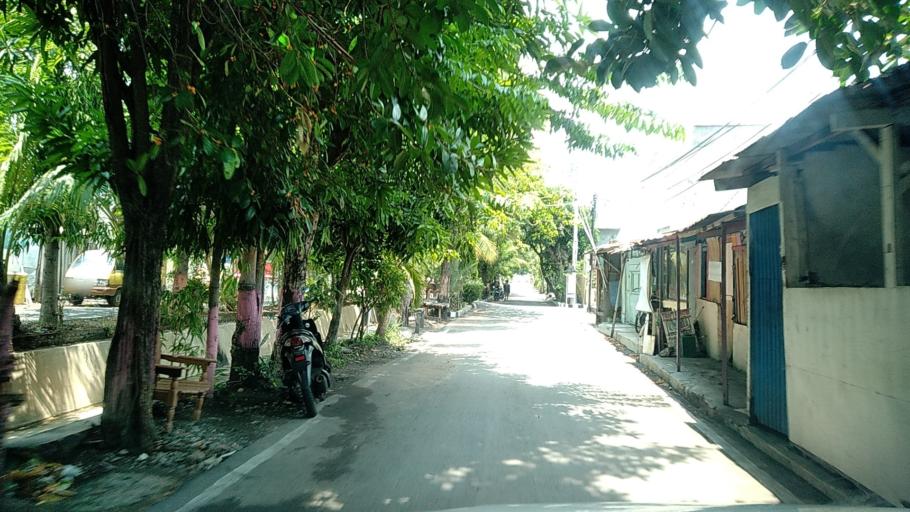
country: ID
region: Central Java
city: Semarang
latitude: -7.0026
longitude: 110.4391
